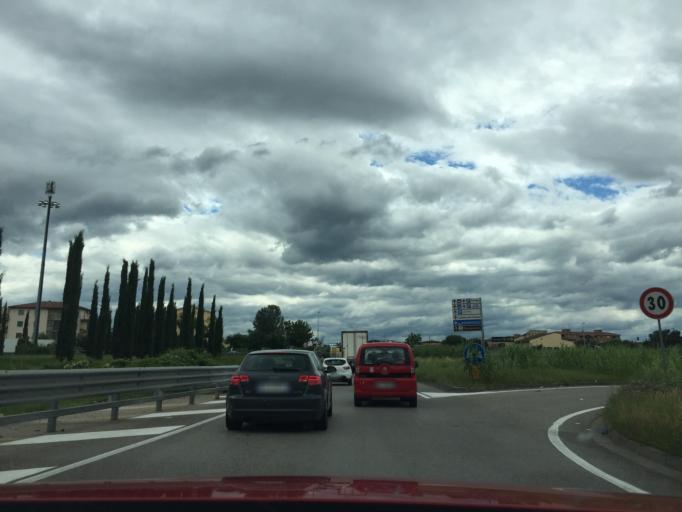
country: IT
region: Tuscany
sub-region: Province of Florence
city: Scandicci
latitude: 43.7697
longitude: 11.1879
